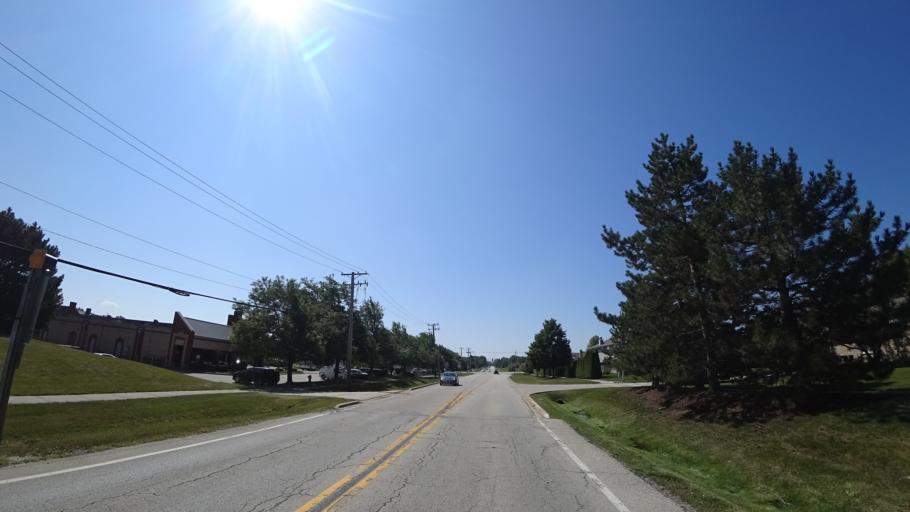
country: US
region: Illinois
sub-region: Cook County
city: Orland Park
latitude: 41.6329
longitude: -87.8198
